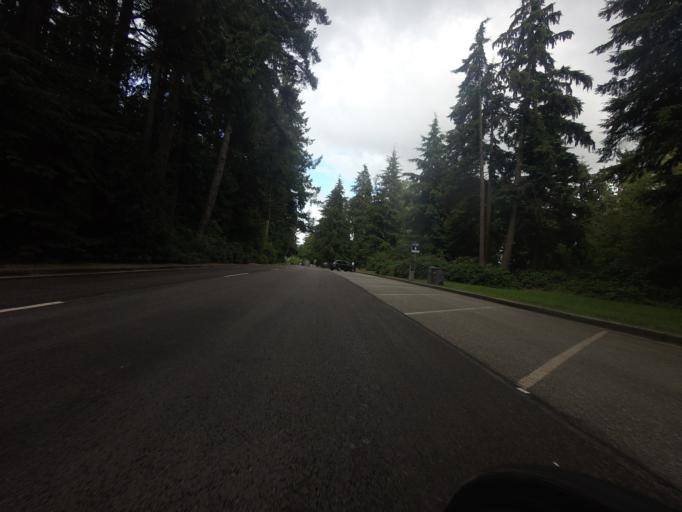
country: CA
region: British Columbia
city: West End
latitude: 49.2968
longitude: -123.1521
